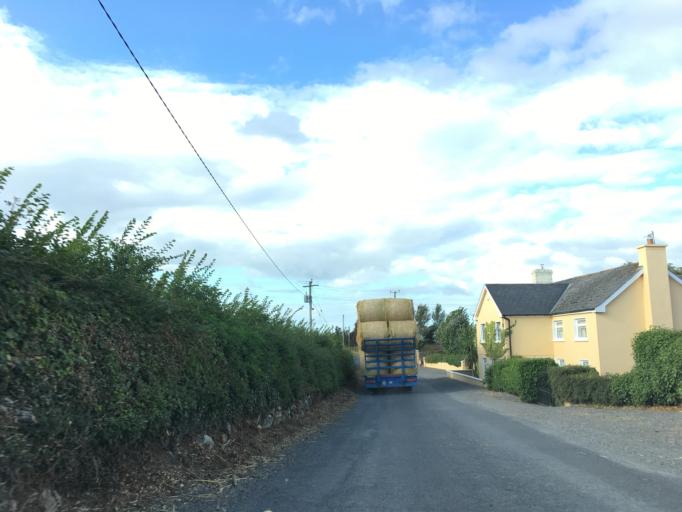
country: IE
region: Munster
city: Cahir
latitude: 52.3013
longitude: -7.9462
